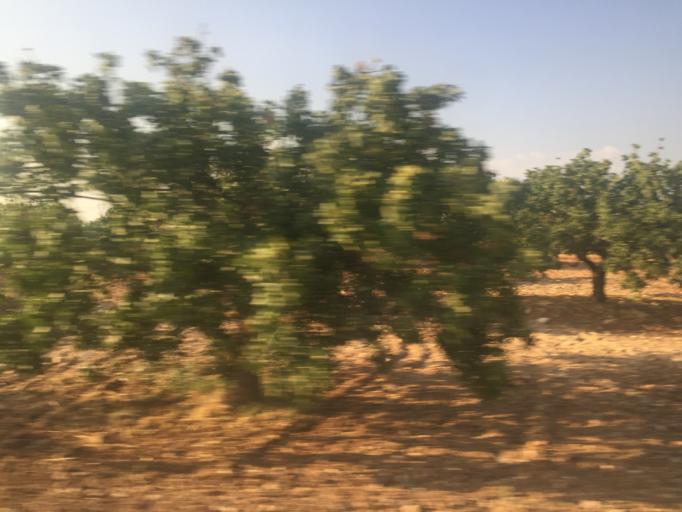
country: TR
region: Gaziantep
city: Nizip
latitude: 37.0142
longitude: 37.8480
